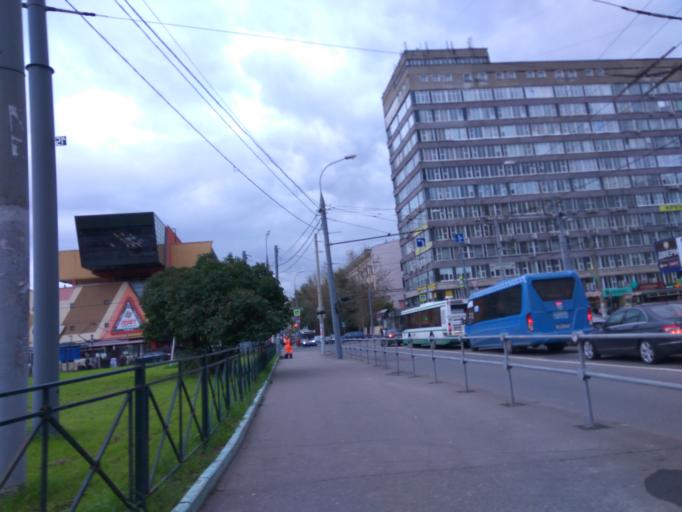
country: RU
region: Moscow
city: Lefortovo
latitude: 55.7818
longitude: 37.7224
